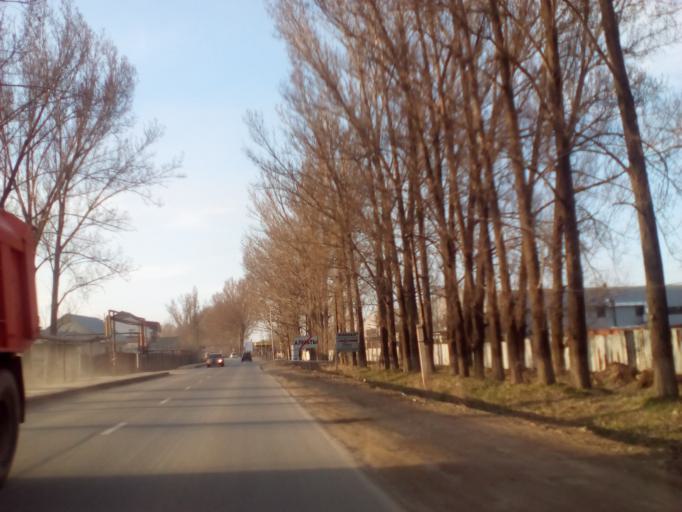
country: KZ
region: Almaty Oblysy
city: Burunday
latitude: 43.2508
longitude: 76.7839
